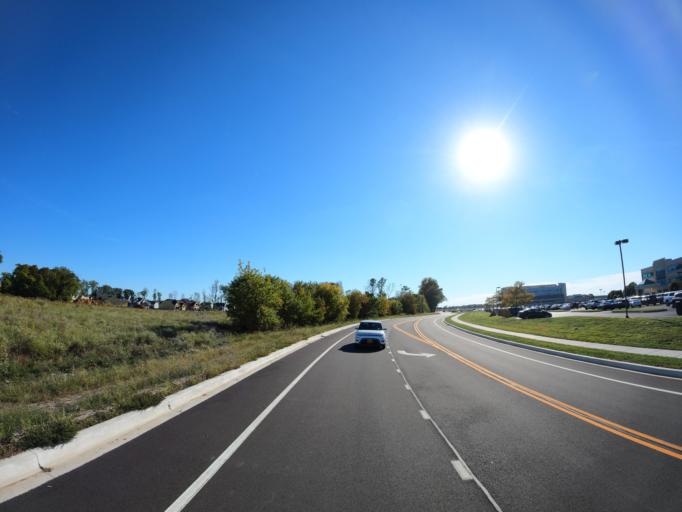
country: US
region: Delaware
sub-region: Sussex County
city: Lewes
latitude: 38.7245
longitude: -75.1365
